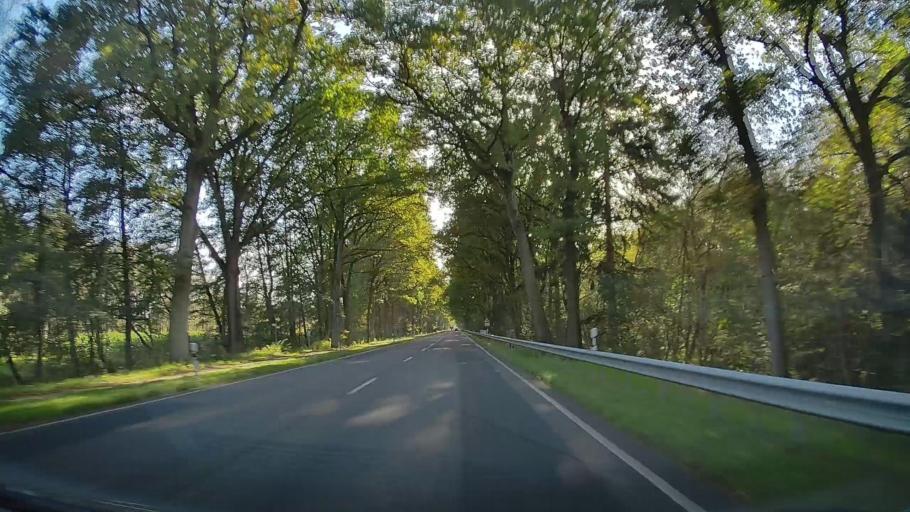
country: DE
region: Lower Saxony
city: Stemmen
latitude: 53.2398
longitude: 9.6039
